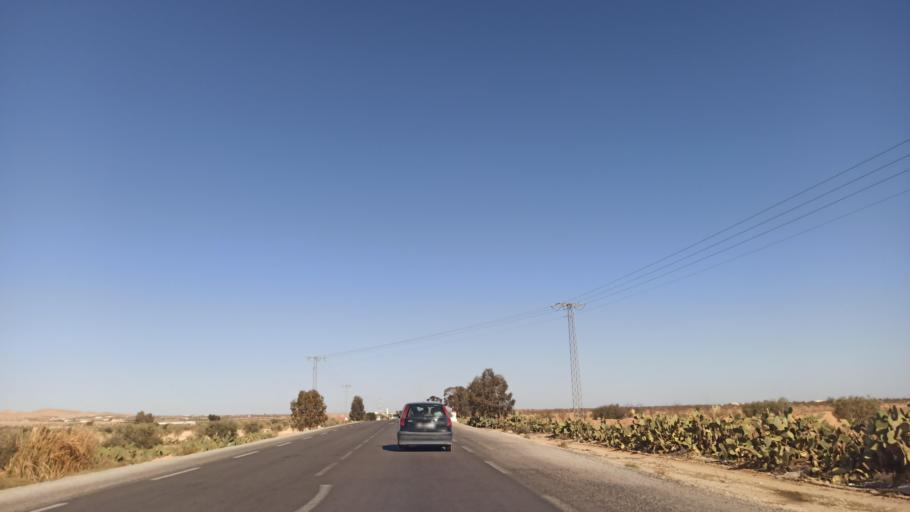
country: TN
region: Sidi Bu Zayd
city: Bi'r al Hufayy
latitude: 34.7267
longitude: 9.0646
